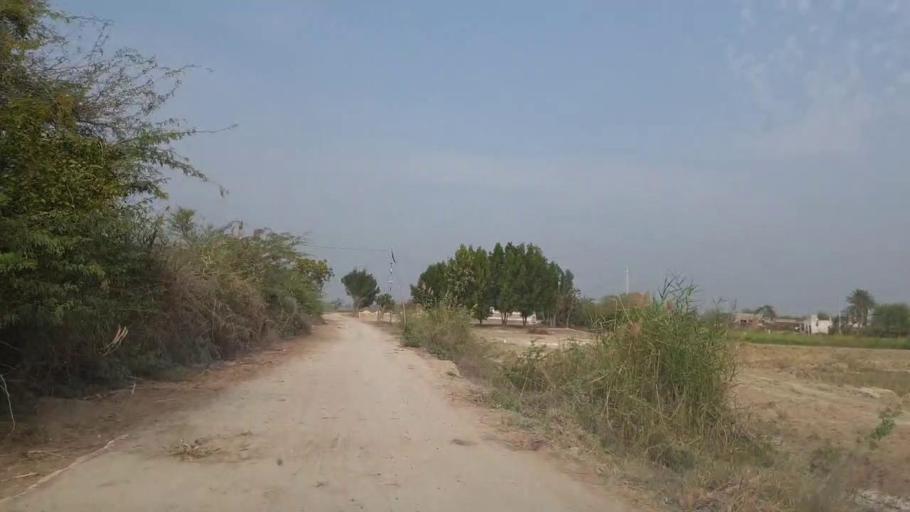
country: PK
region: Sindh
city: Mirpur Khas
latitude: 25.5419
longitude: 69.1341
